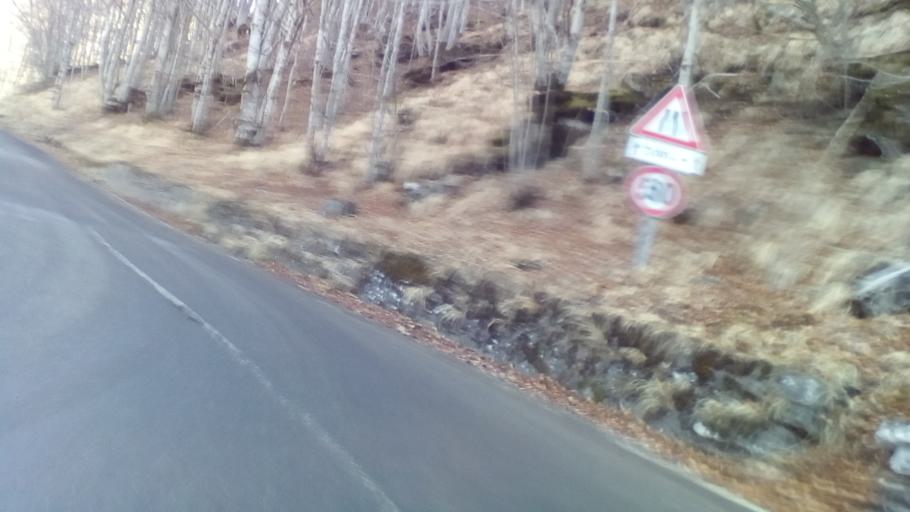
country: IT
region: Emilia-Romagna
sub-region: Provincia di Modena
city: Pievepelago
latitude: 44.1864
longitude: 10.5654
